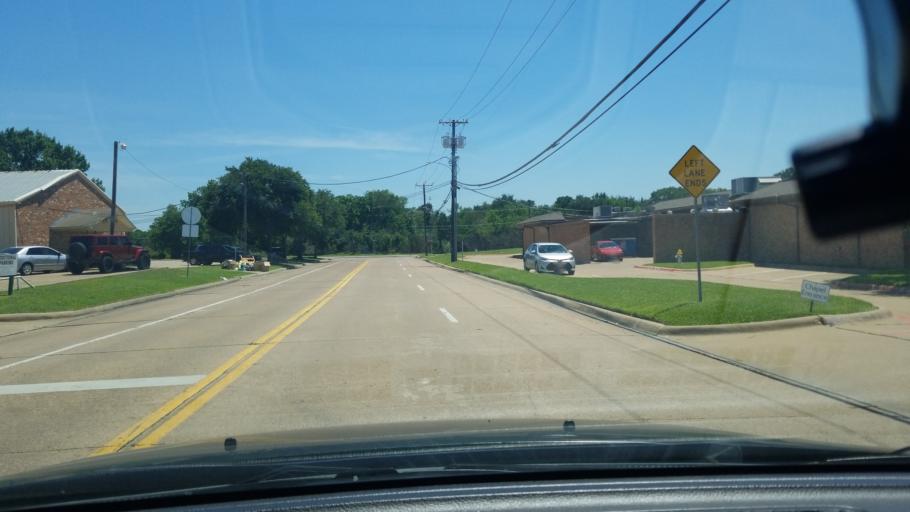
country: US
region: Texas
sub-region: Dallas County
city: Mesquite
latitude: 32.7684
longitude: -96.6127
